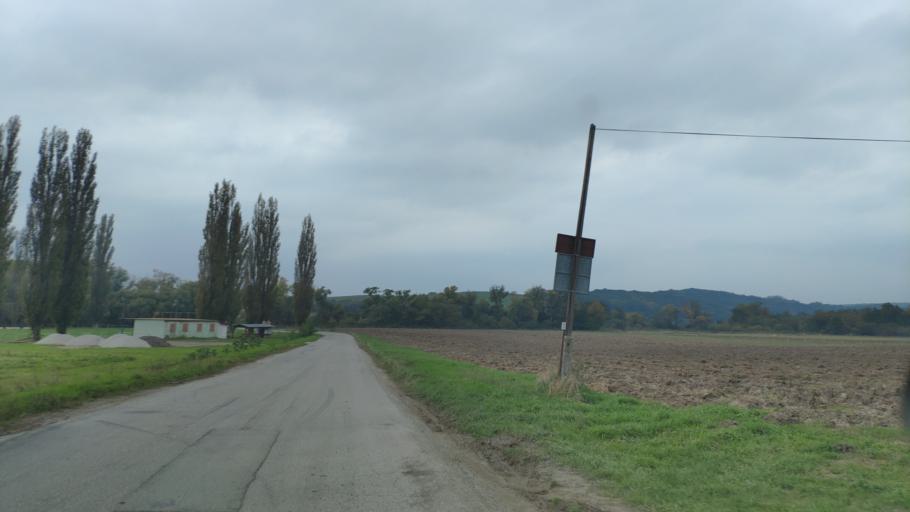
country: SK
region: Kosicky
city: Kosice
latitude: 48.6371
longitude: 21.3794
